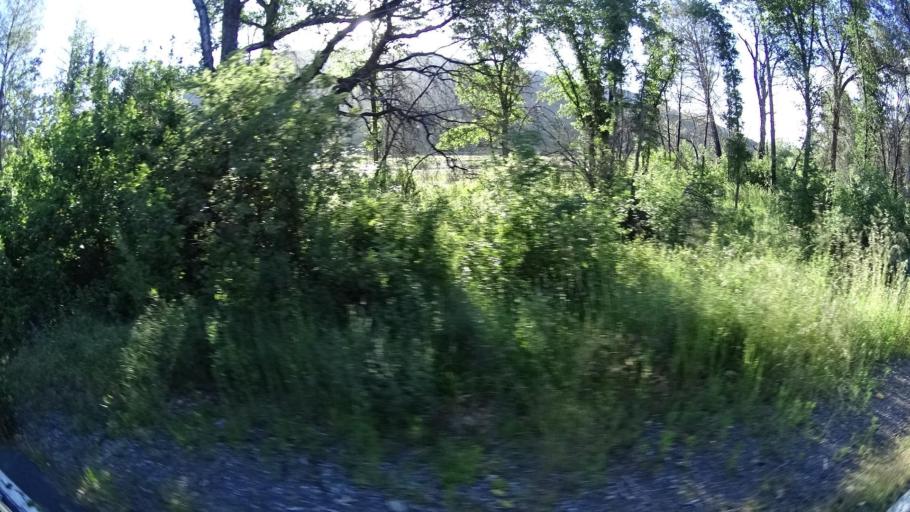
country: US
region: California
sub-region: Lake County
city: Upper Lake
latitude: 39.2282
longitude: -122.9439
